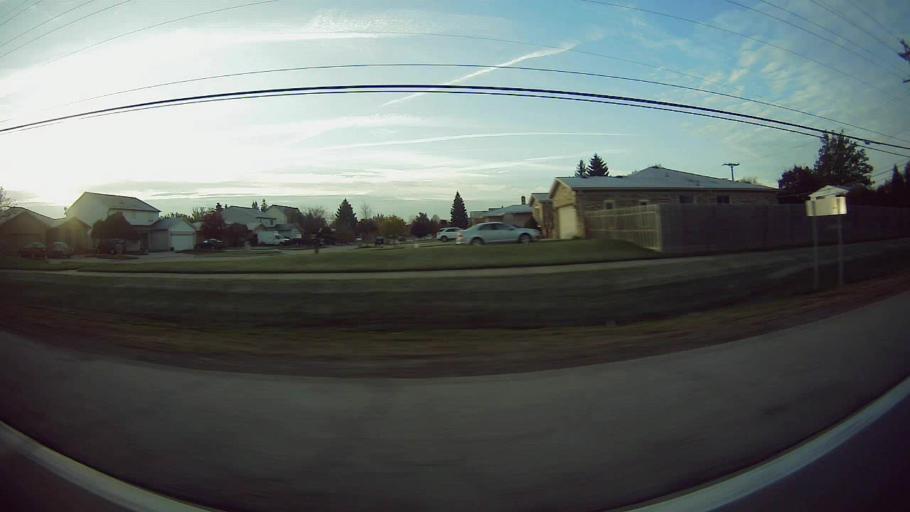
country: US
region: Michigan
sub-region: Macomb County
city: Sterling Heights
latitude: 42.5670
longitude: -82.9899
